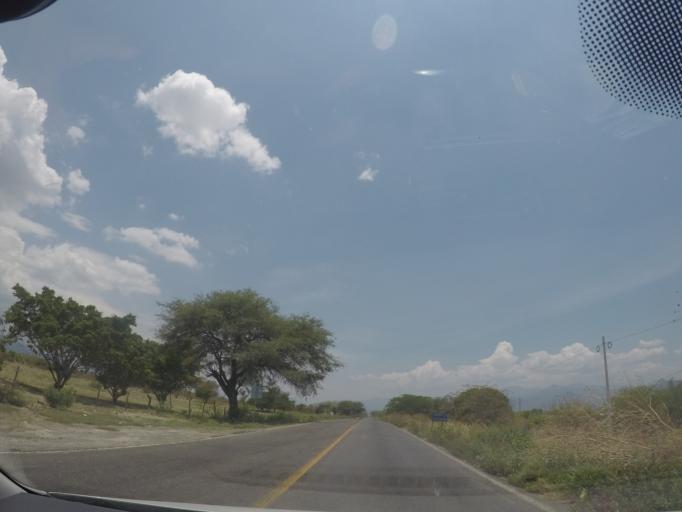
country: MX
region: Oaxaca
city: Santa Maria Jalapa del Marques
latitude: 16.4398
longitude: -95.4667
